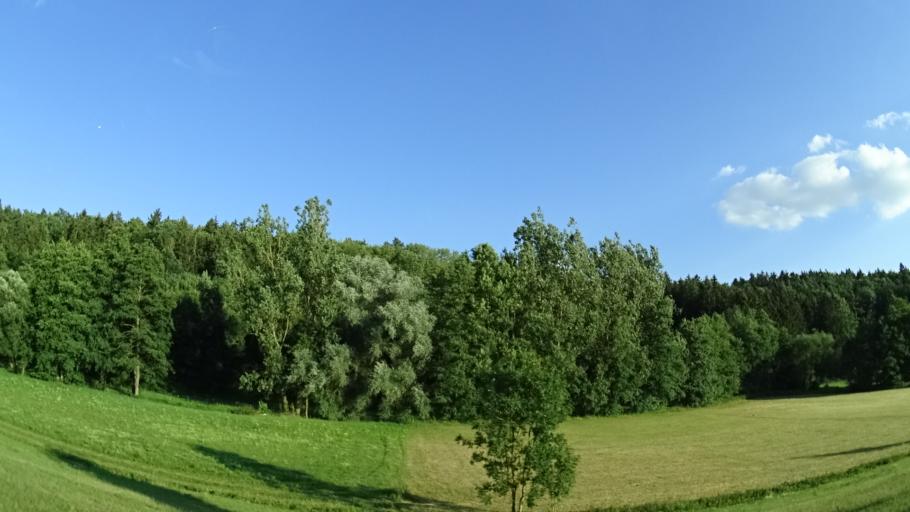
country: DE
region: Bavaria
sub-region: Regierungsbezirk Unterfranken
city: Mellrichstadt
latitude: 50.4453
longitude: 10.3275
